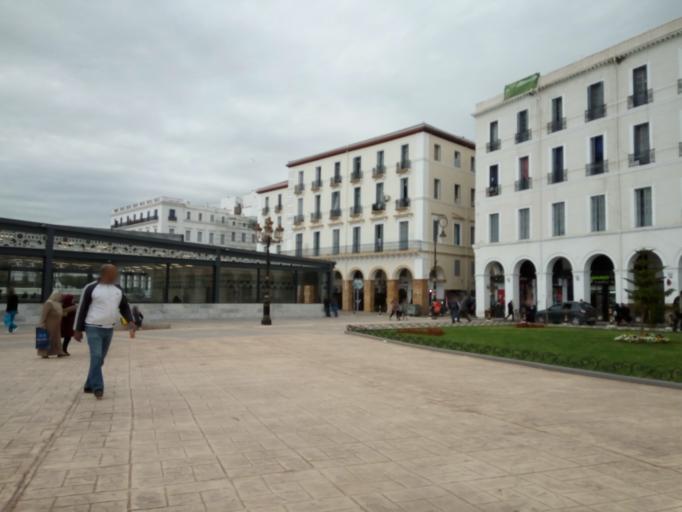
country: DZ
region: Alger
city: Algiers
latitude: 36.7856
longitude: 3.0624
